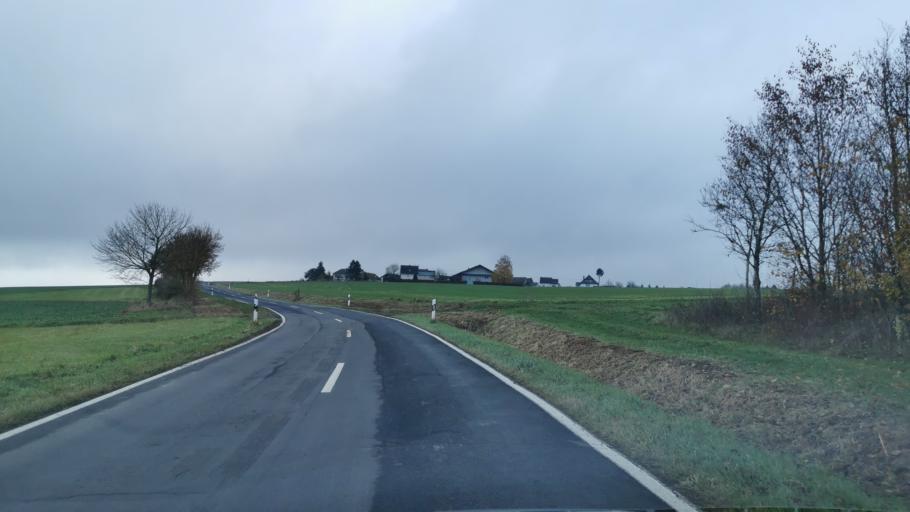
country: DE
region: Rheinland-Pfalz
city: Greimersburg
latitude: 50.1832
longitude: 7.1494
